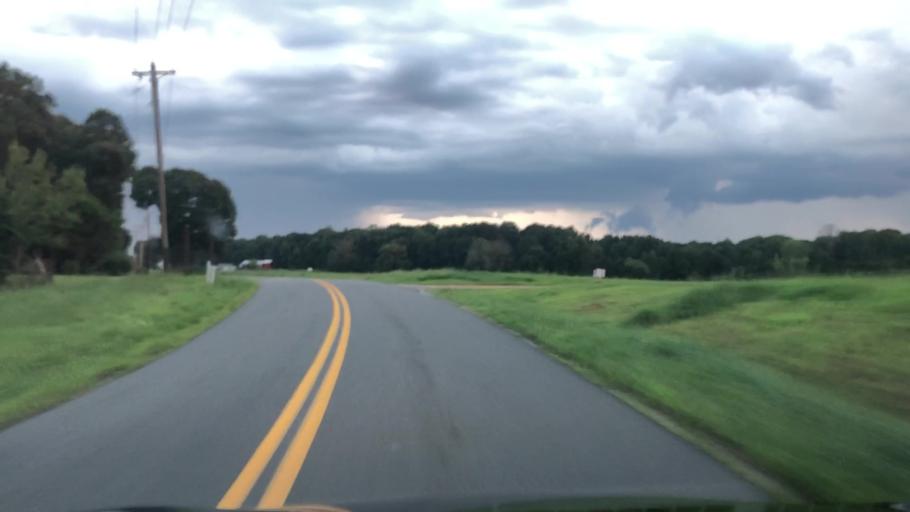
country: US
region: Virginia
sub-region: Stafford County
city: Falmouth
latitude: 38.4433
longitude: -77.5911
